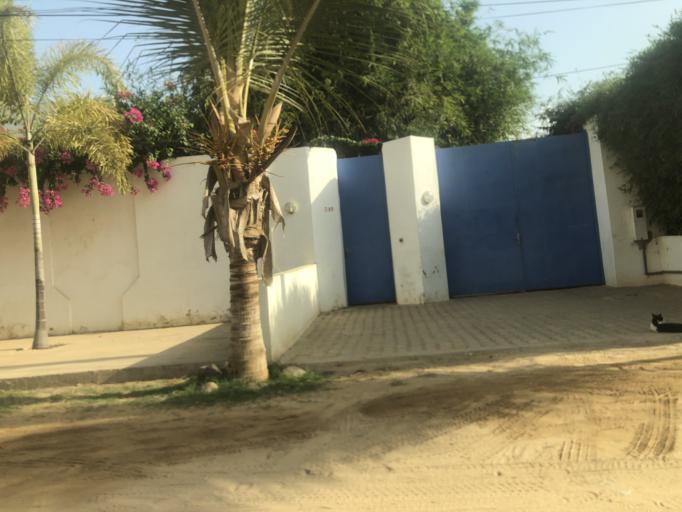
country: SN
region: Dakar
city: Mermoz Boabab
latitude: 14.7419
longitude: -17.5137
